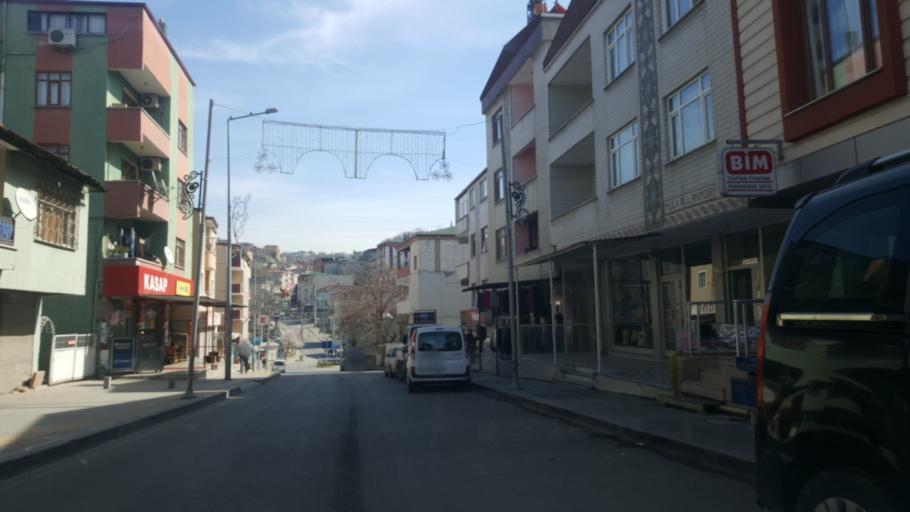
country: TR
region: Kocaeli
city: Tavsancil
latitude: 40.7853
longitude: 29.5448
